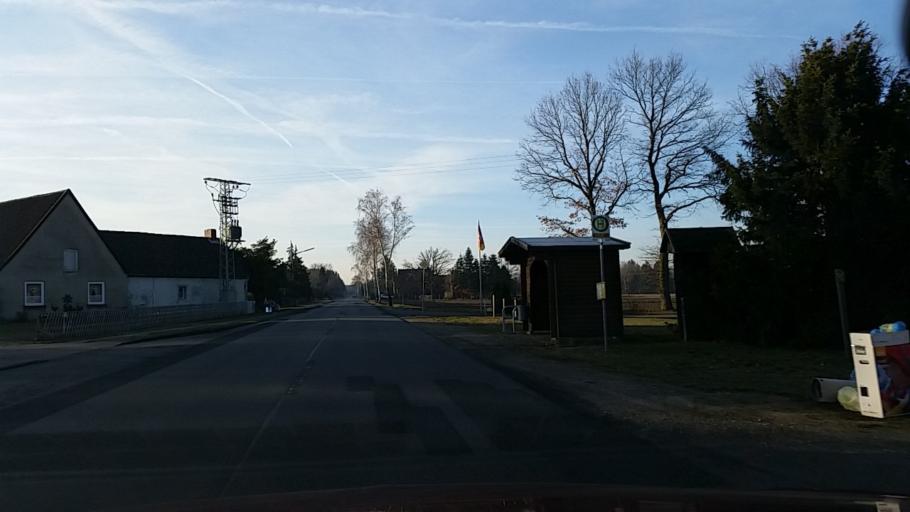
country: DE
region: Lower Saxony
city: Schoneworde
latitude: 52.6239
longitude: 10.6892
